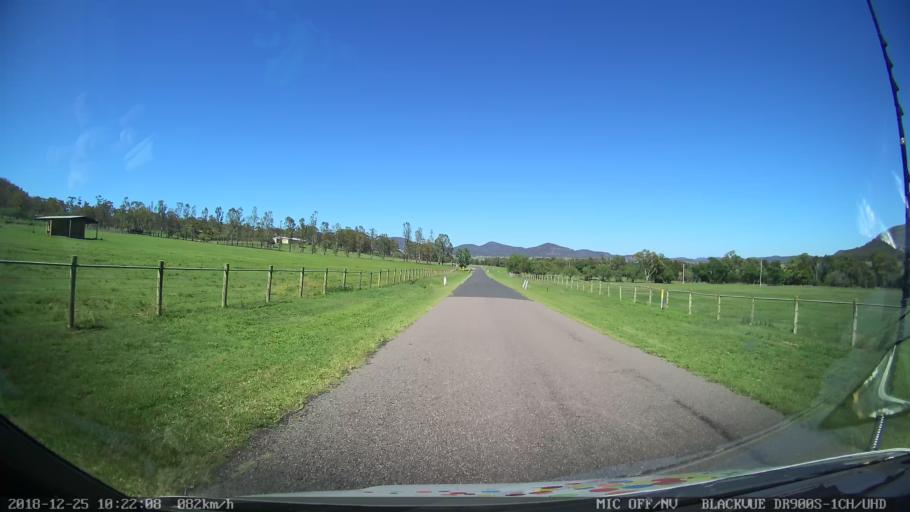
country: AU
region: New South Wales
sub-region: Muswellbrook
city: Denman
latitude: -32.3743
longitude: 150.5359
